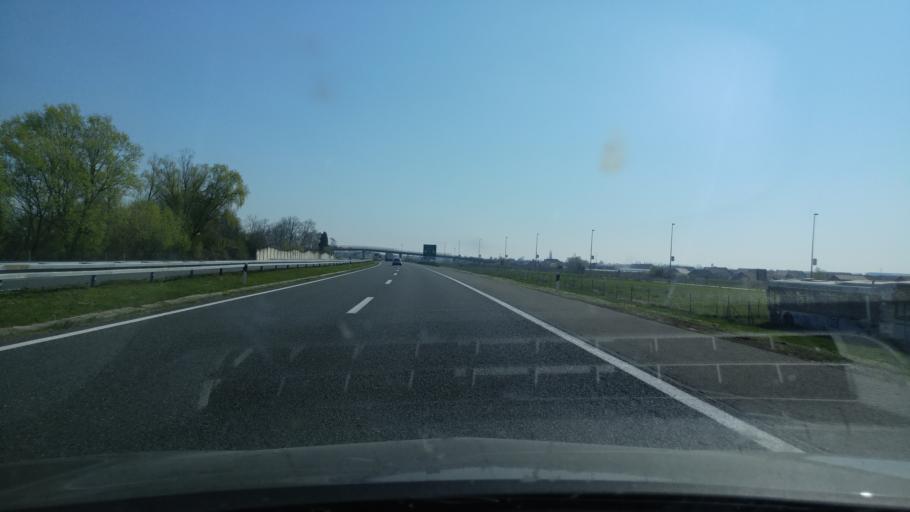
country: HR
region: Brodsko-Posavska
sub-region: Grad Slavonski Brod
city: Slavonski Brod
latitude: 45.1794
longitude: 17.9919
